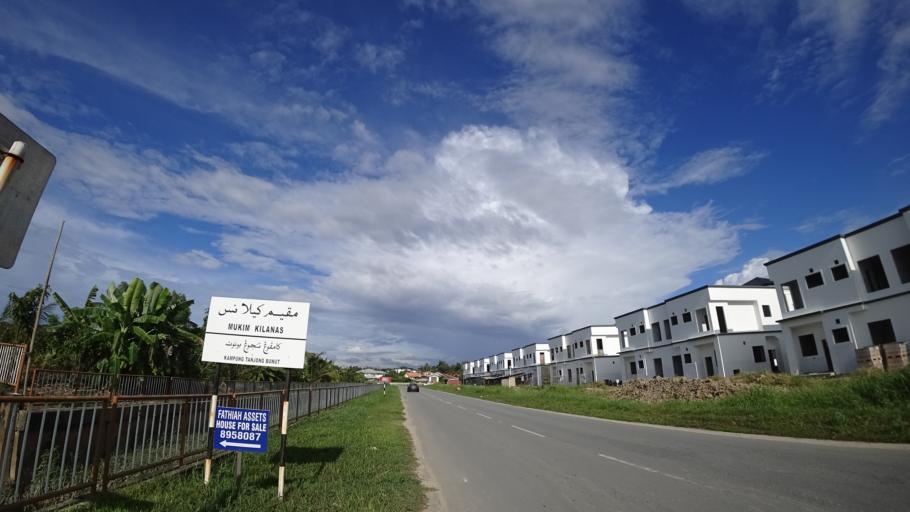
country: BN
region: Brunei and Muara
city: Bandar Seri Begawan
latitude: 4.8842
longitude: 114.8534
